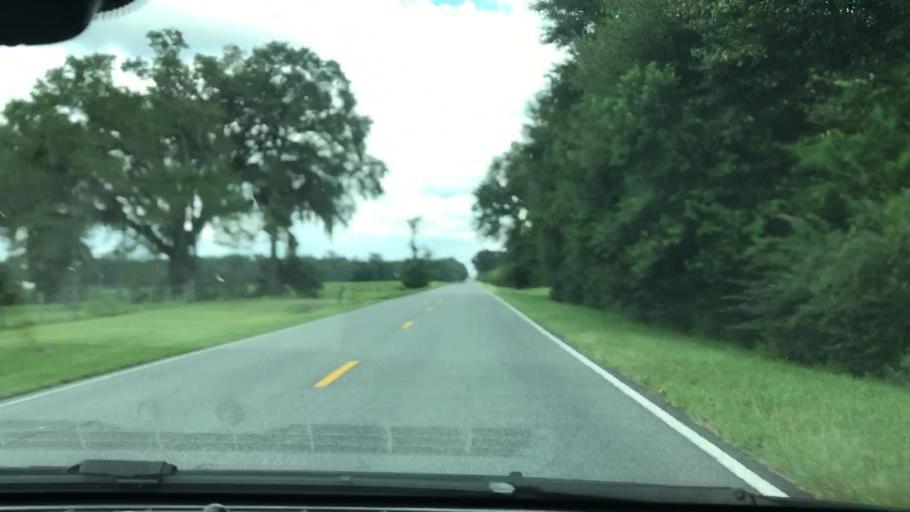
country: US
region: Florida
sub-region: Jackson County
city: Malone
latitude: 30.8863
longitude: -85.1548
